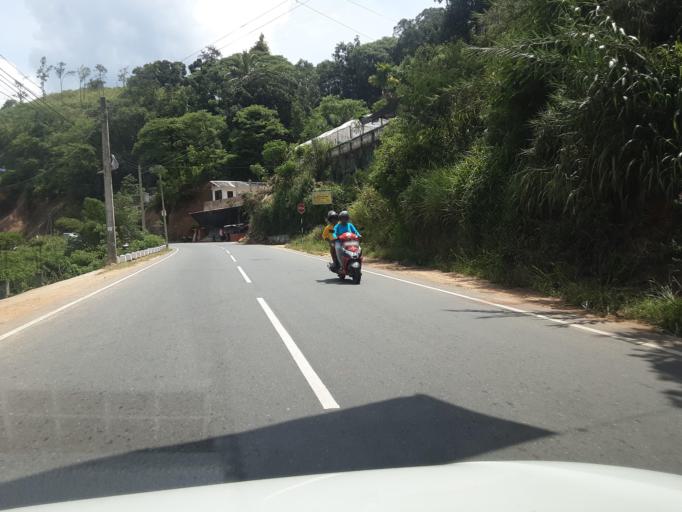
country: LK
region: Central
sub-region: Nuwara Eliya District
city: Nuwara Eliya
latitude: 6.9160
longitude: 80.9058
